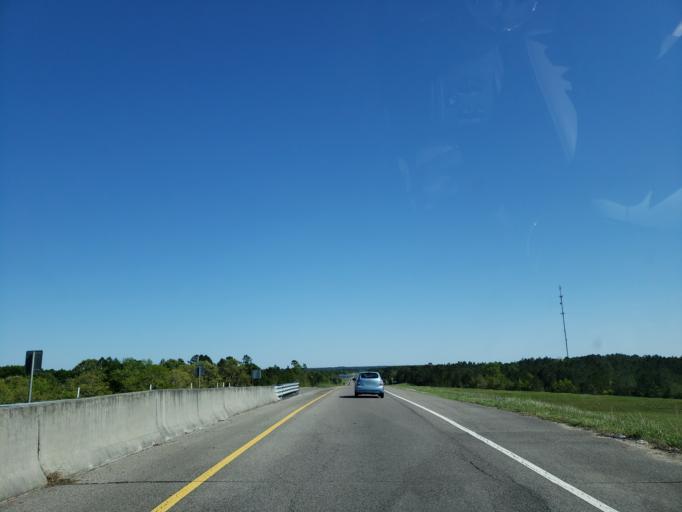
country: US
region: Mississippi
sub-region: Harrison County
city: Saucier
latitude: 30.6530
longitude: -89.1330
